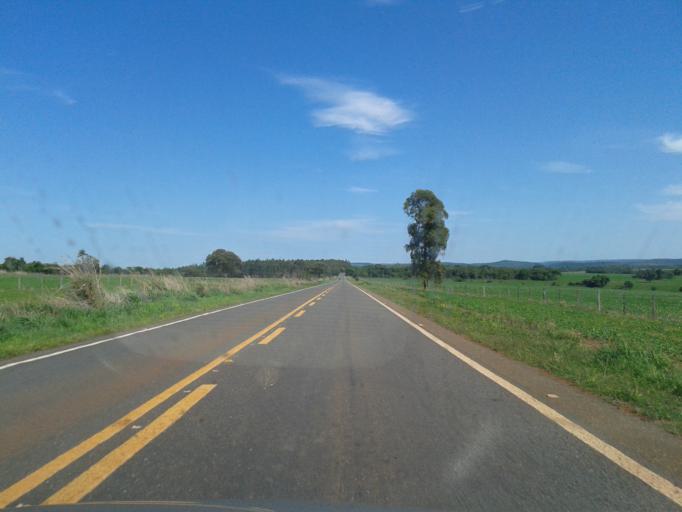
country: BR
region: Goias
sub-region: Piracanjuba
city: Piracanjuba
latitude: -17.3386
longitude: -48.7945
